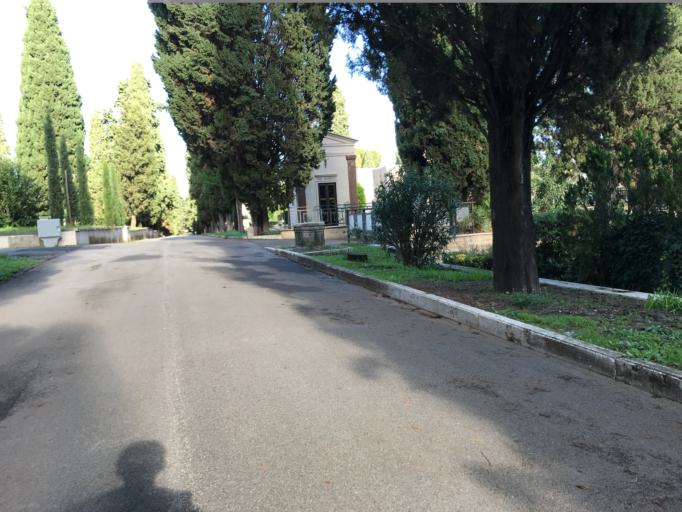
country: IT
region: Latium
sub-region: Citta metropolitana di Roma Capitale
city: Rome
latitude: 41.9047
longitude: 12.5318
